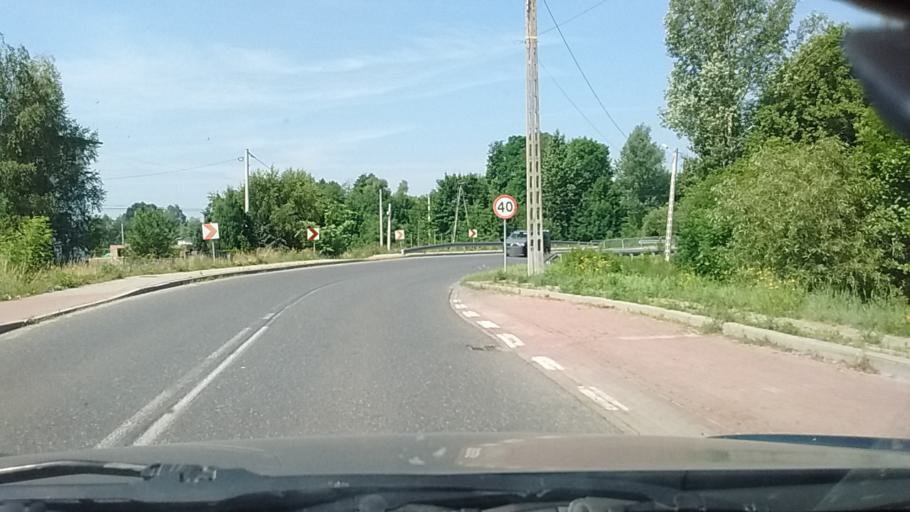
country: PL
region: Subcarpathian Voivodeship
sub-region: Powiat lancucki
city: Sonina
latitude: 50.0561
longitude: 22.2689
